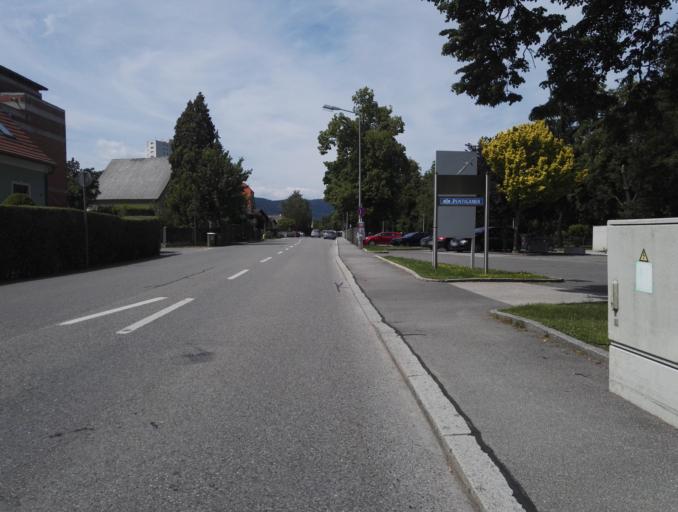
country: AT
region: Styria
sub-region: Graz Stadt
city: Wetzelsdorf
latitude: 47.0377
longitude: 15.4162
